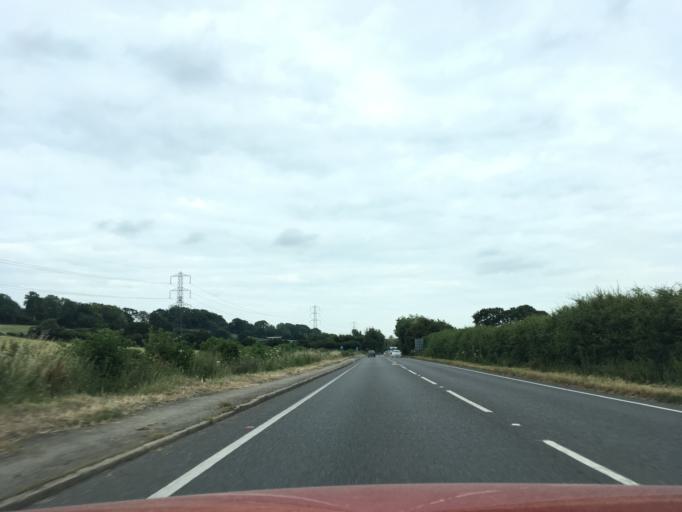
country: GB
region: England
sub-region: Central Bedfordshire
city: Kensworth
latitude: 51.8637
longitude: -0.4853
